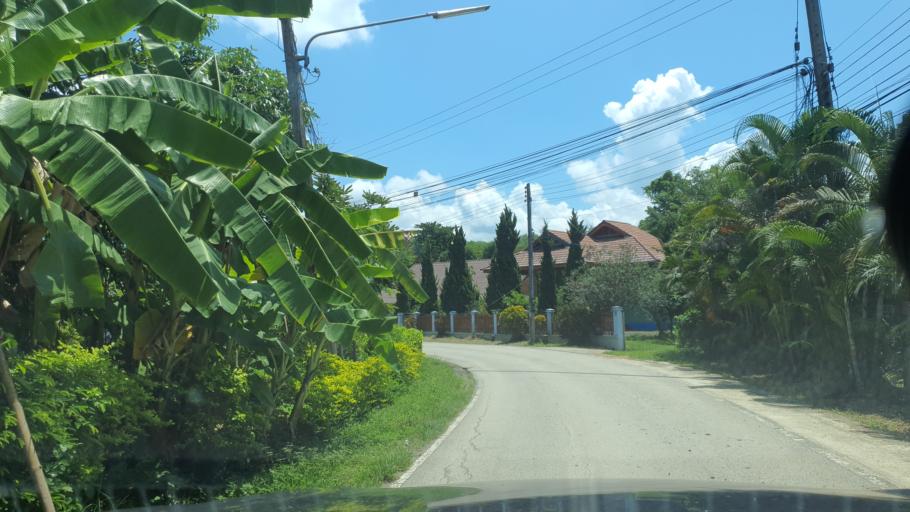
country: TH
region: Chiang Mai
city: Mae On
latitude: 18.8139
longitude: 99.2586
